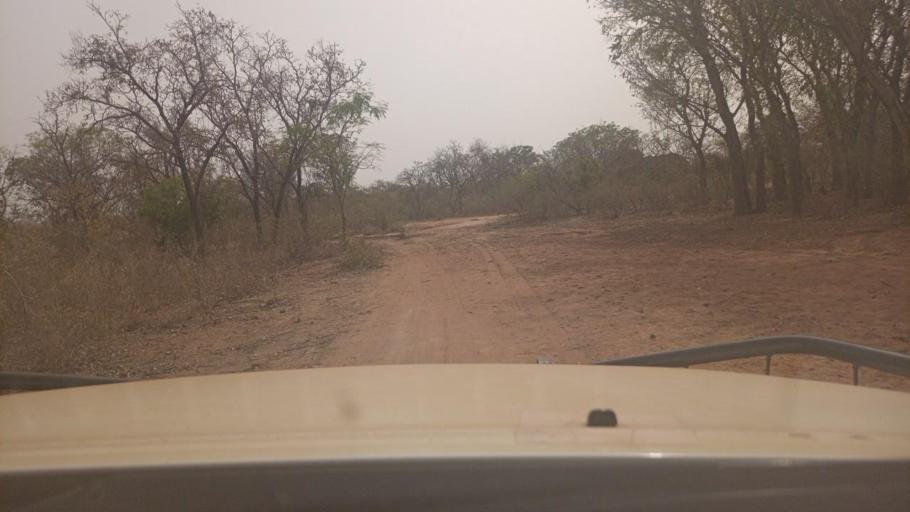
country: BF
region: Boucle du Mouhoun
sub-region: Province des Banwa
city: Salanso
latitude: 12.1589
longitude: -4.2442
